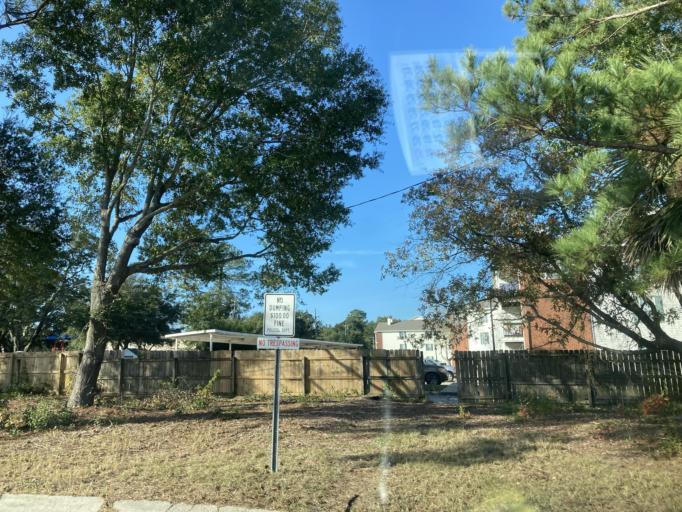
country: US
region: Mississippi
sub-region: Harrison County
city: D'Iberville
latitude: 30.4036
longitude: -88.9635
